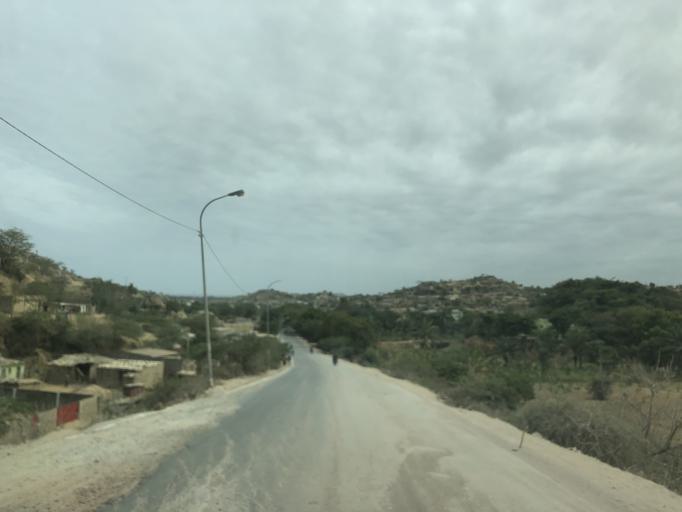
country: AO
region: Cuanza Sul
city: Sumbe
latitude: -11.2208
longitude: 13.8476
